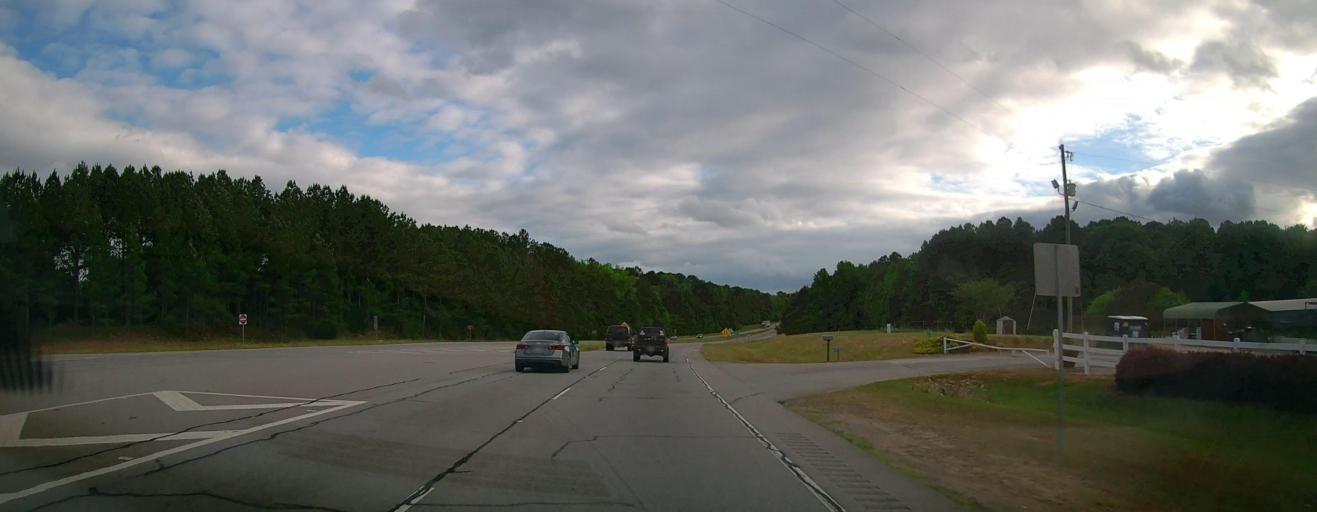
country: US
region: Georgia
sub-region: Oconee County
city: Watkinsville
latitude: 33.8463
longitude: -83.4229
